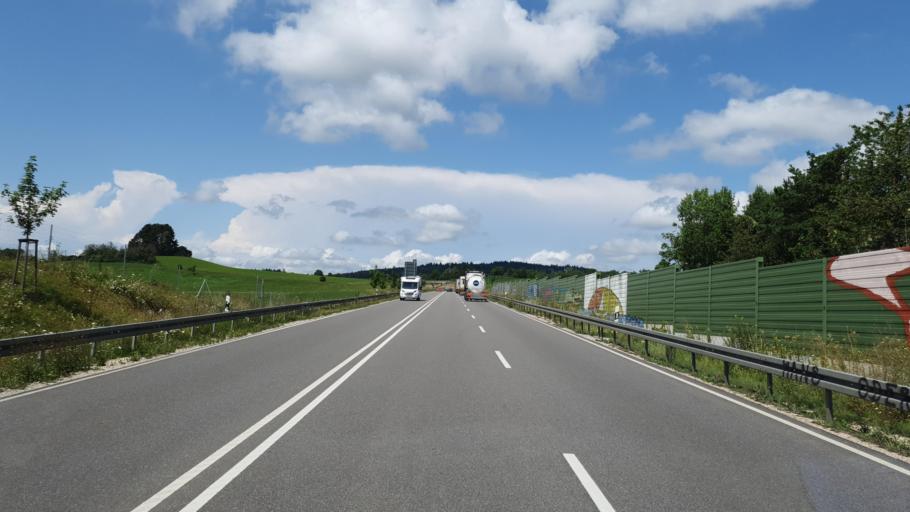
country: DE
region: Baden-Wuerttemberg
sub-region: Tuebingen Region
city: Uberlingen
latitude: 47.7843
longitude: 9.1731
